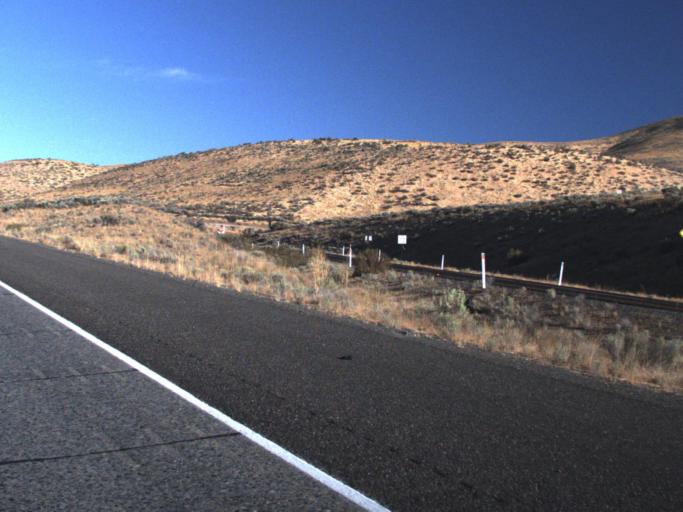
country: US
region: Washington
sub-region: Kittitas County
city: Kittitas
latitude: 46.8440
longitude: -120.3761
